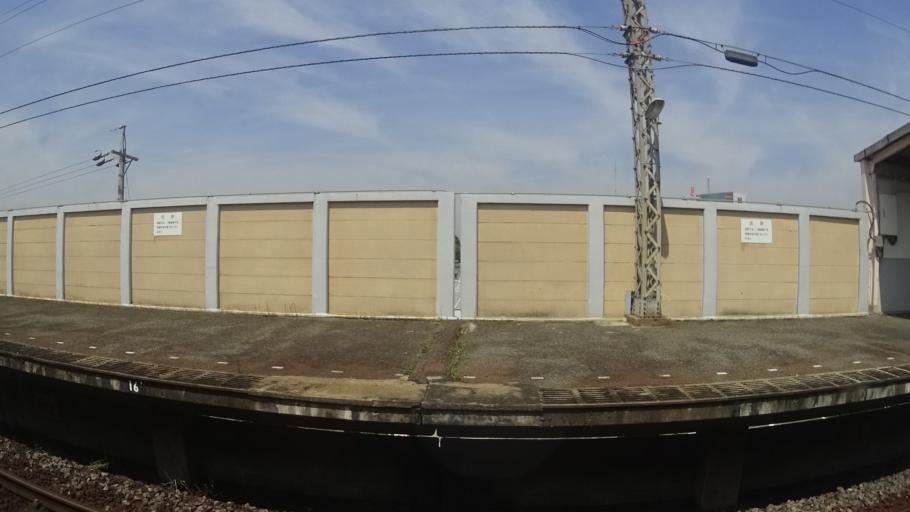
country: JP
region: Mie
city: Suzuka
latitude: 34.8783
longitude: 136.5888
